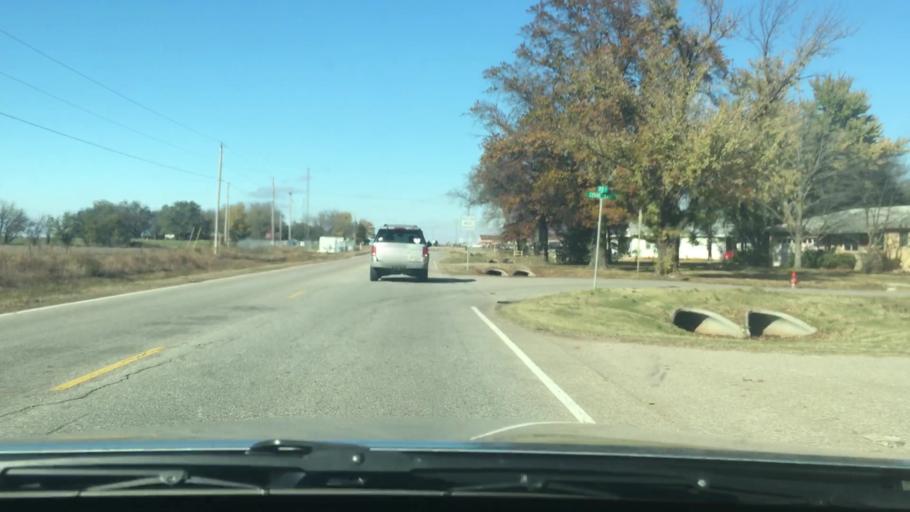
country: US
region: Kansas
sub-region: Sedgwick County
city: Maize
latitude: 37.7642
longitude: -97.4808
